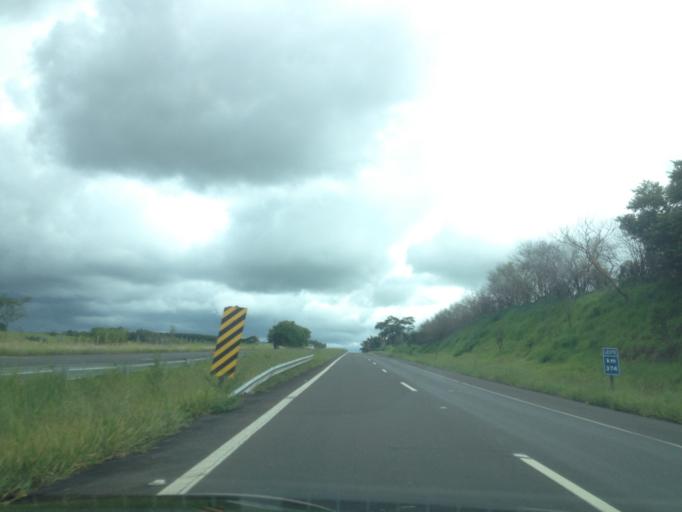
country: BR
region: Sao Paulo
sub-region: Duartina
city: Duartina
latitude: -22.3263
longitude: -49.3161
